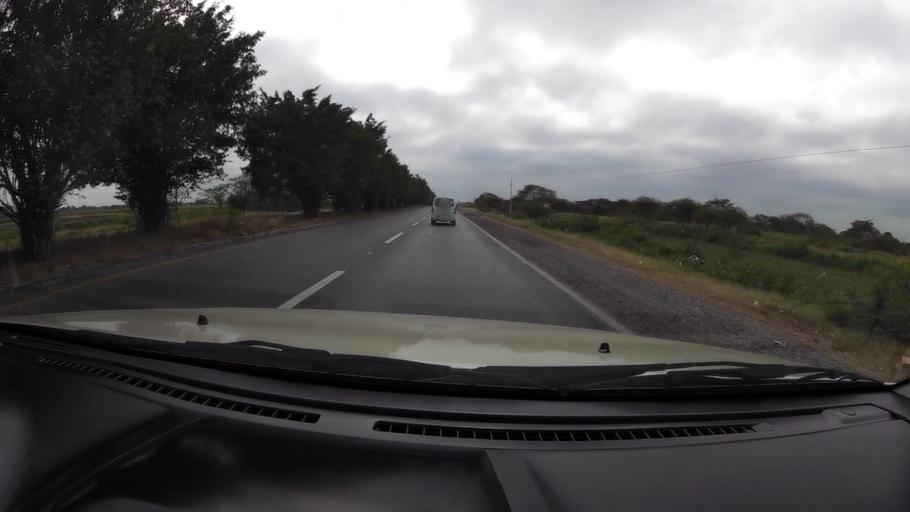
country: EC
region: Guayas
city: Yaguachi Nuevo
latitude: -2.2094
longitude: -79.7321
